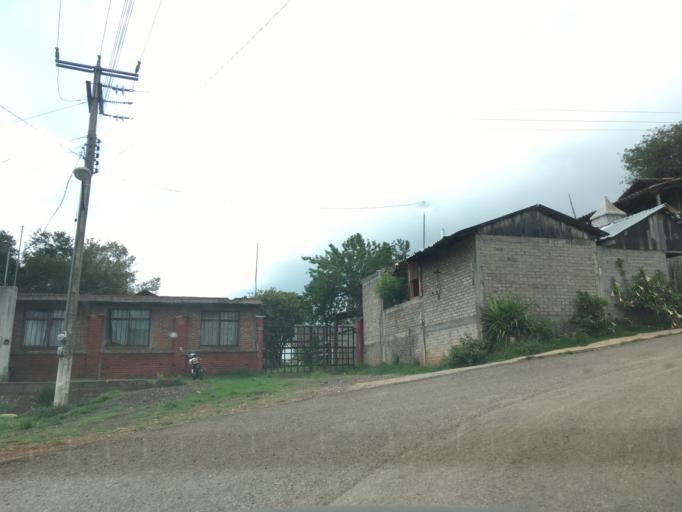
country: MX
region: Michoacan
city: Acuitzio del Canje
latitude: 19.5056
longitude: -101.2174
